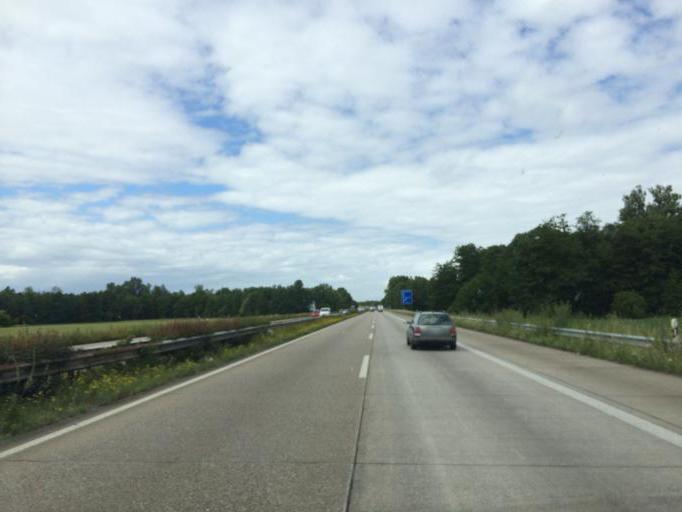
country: DE
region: North Rhine-Westphalia
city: Kempen
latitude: 51.4095
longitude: 6.4351
